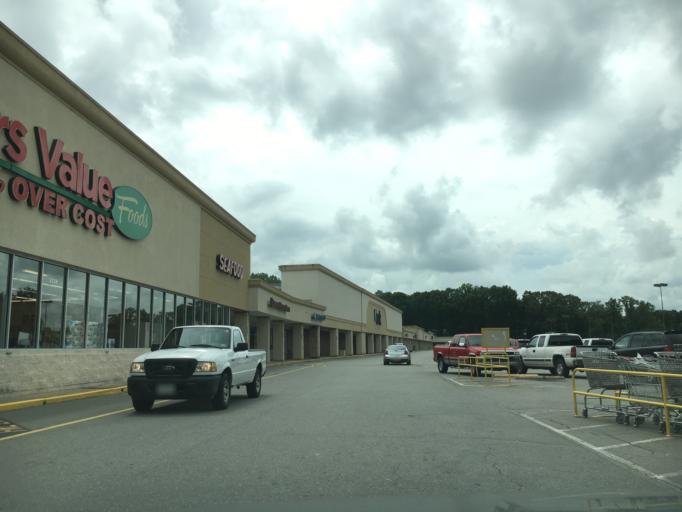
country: US
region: Virginia
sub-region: Halifax County
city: South Boston
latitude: 36.7149
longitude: -78.9125
